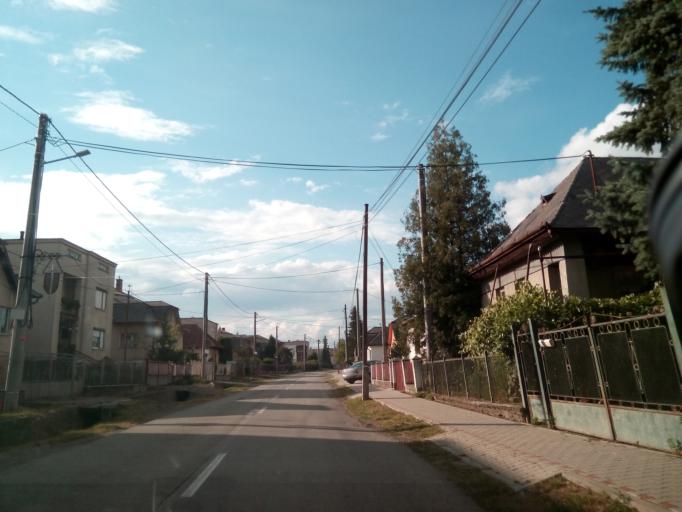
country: SK
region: Kosicky
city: Secovce
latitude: 48.5841
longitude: 21.5678
